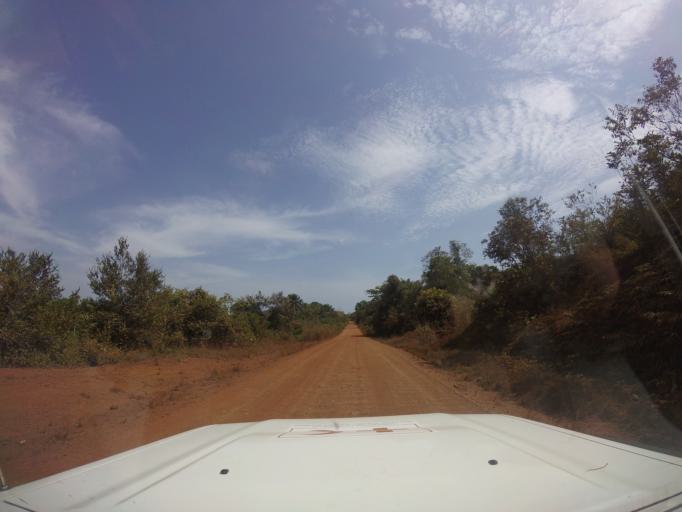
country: LR
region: Grand Cape Mount
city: Robertsport
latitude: 6.7137
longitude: -11.3359
